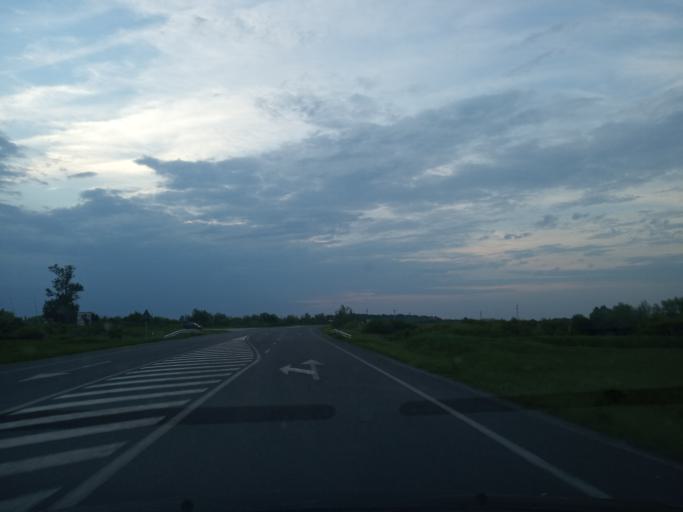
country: RO
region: Timis
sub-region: Oras Deta
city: Deta
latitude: 45.3735
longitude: 21.2349
